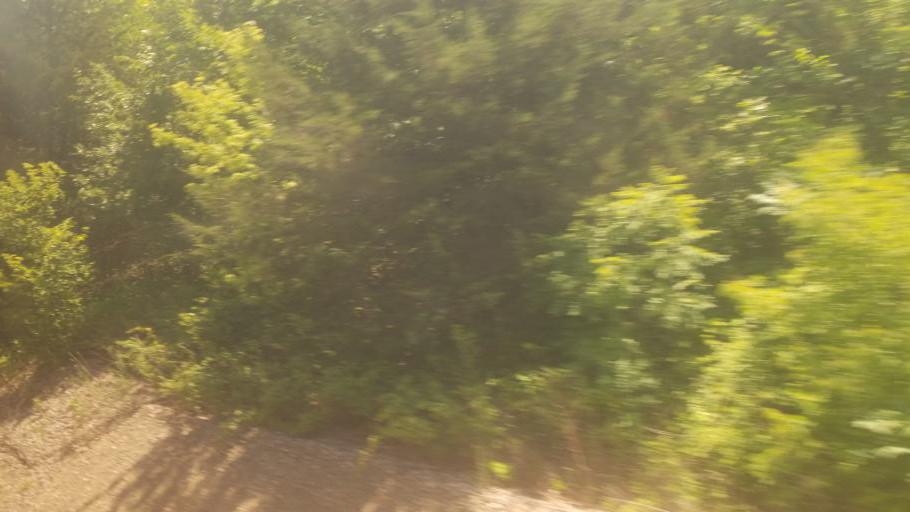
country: US
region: Missouri
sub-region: Linn County
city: Marceline
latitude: 39.8267
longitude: -92.8332
